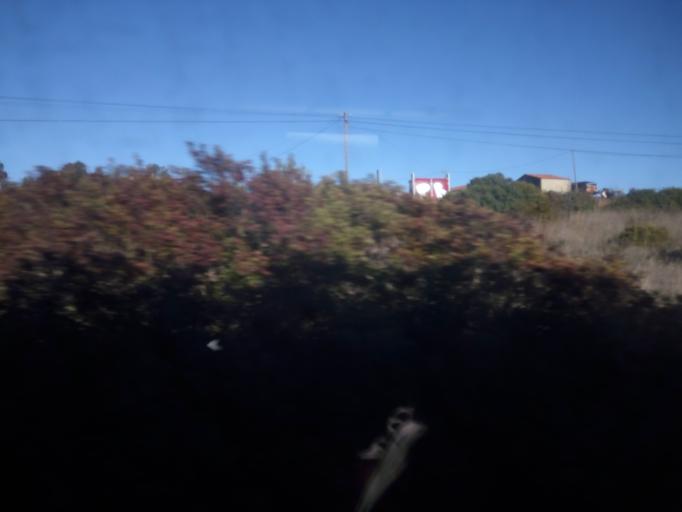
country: PT
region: Faro
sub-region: Silves
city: Sao Bartolomeu de Messines
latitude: 37.3205
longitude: -8.3301
